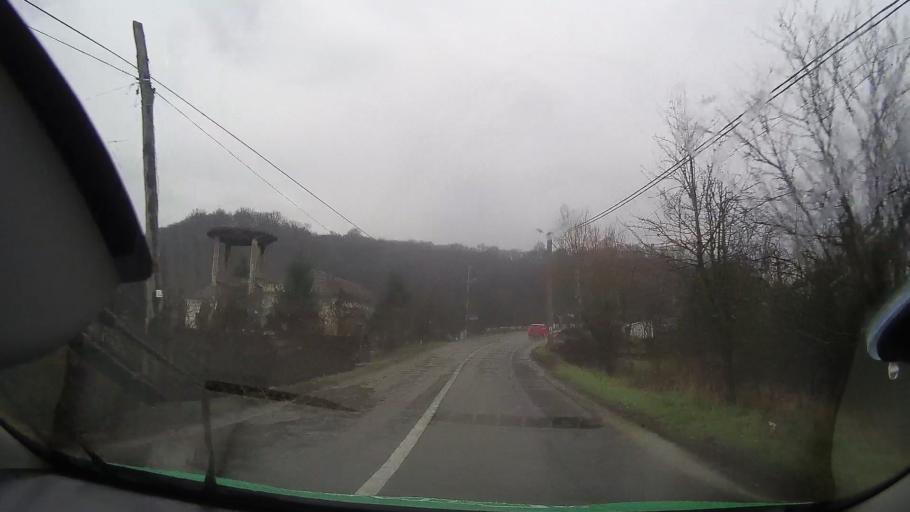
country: RO
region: Bihor
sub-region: Comuna Holod
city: Holod
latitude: 46.7808
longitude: 22.1349
